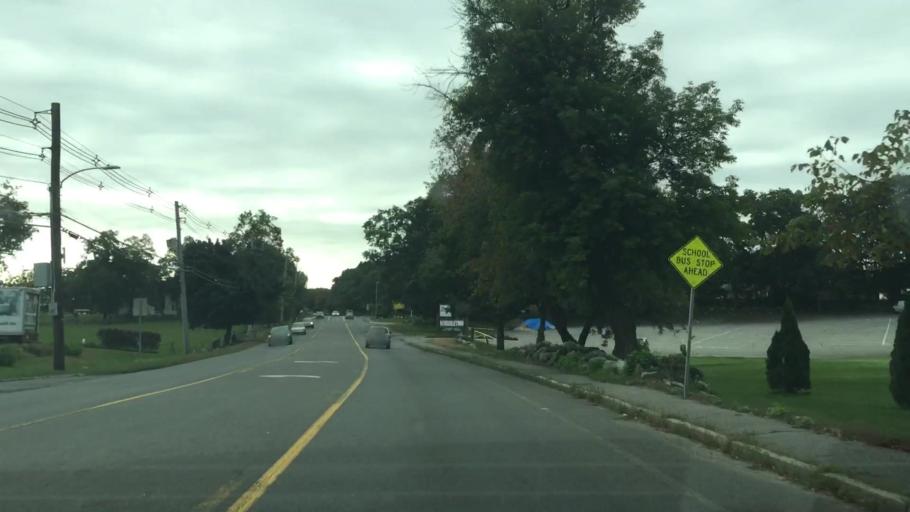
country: US
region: Massachusetts
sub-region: Essex County
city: Middleton
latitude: 42.5884
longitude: -71.0116
